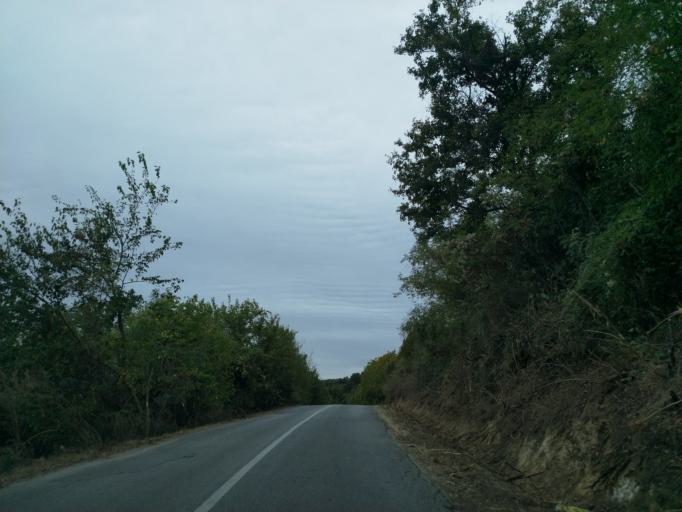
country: RS
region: Central Serbia
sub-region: Pomoravski Okrug
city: Paracin
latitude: 43.8539
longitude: 21.3239
